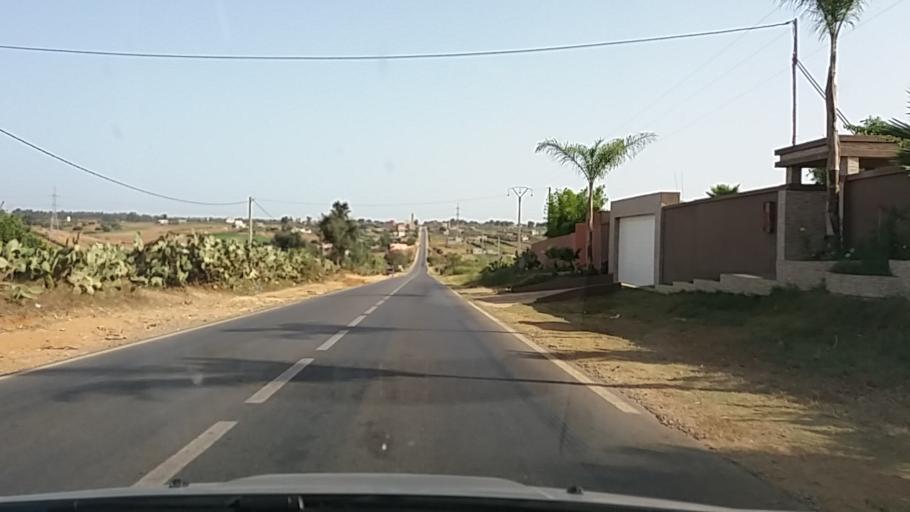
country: MA
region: Gharb-Chrarda-Beni Hssen
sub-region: Kenitra Province
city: Kenitra
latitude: 34.1134
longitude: -6.5594
